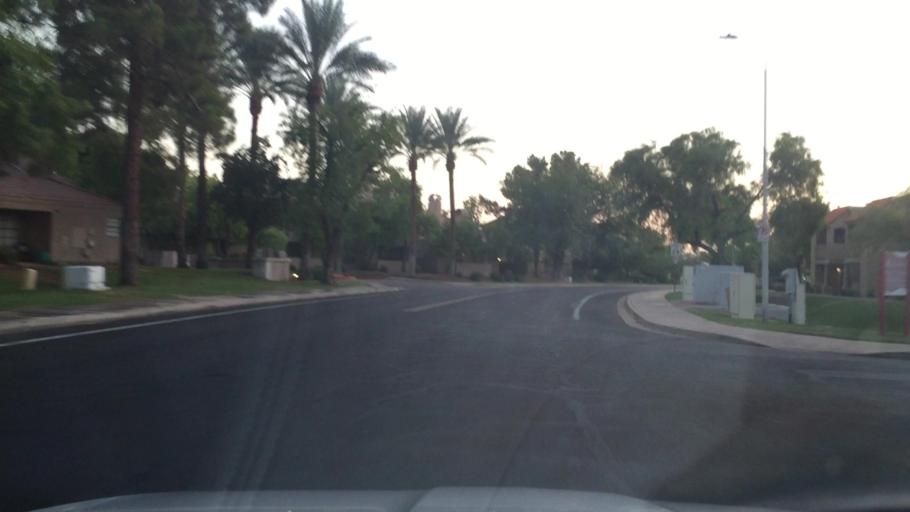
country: US
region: Arizona
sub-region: Maricopa County
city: Scottsdale
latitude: 33.5215
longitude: -111.9135
